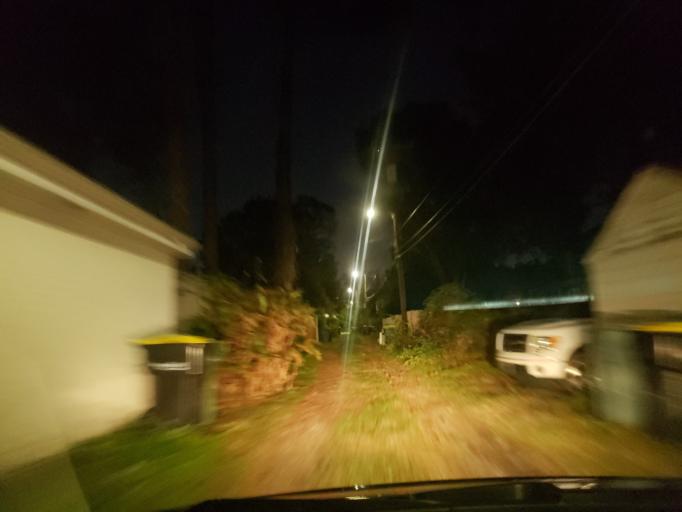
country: US
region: Georgia
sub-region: Chatham County
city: Savannah
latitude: 32.0456
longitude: -81.0896
